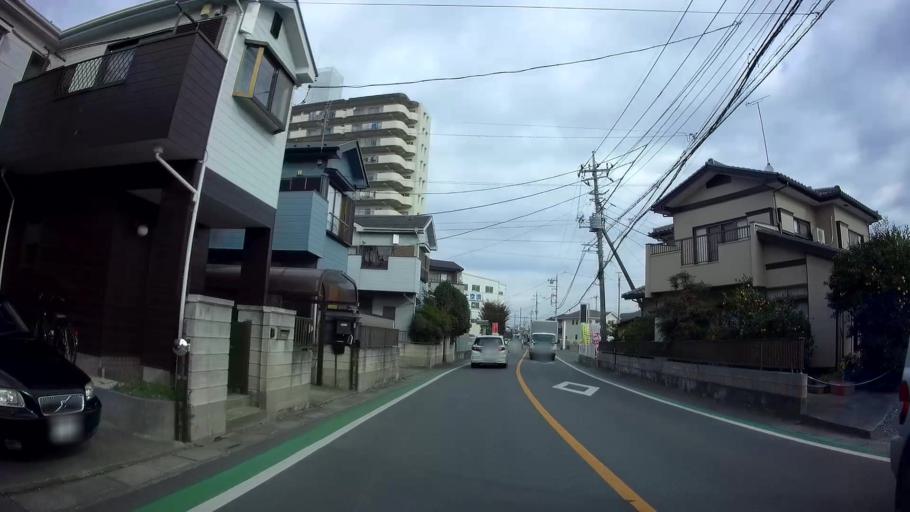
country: JP
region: Saitama
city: Konosu
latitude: 36.0450
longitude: 139.5208
